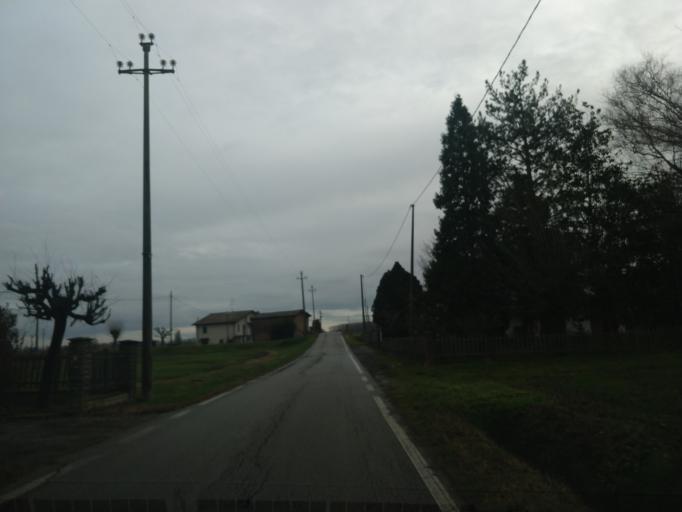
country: IT
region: Emilia-Romagna
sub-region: Provincia di Ferrara
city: Corpo Reno
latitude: 44.7562
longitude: 11.3204
